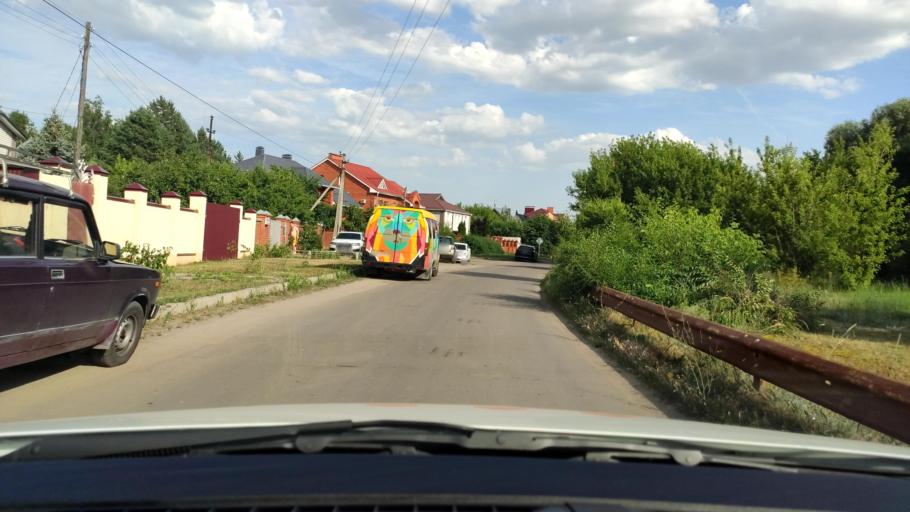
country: RU
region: Voronezj
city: Novaya Usman'
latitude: 51.6287
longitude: 39.4207
